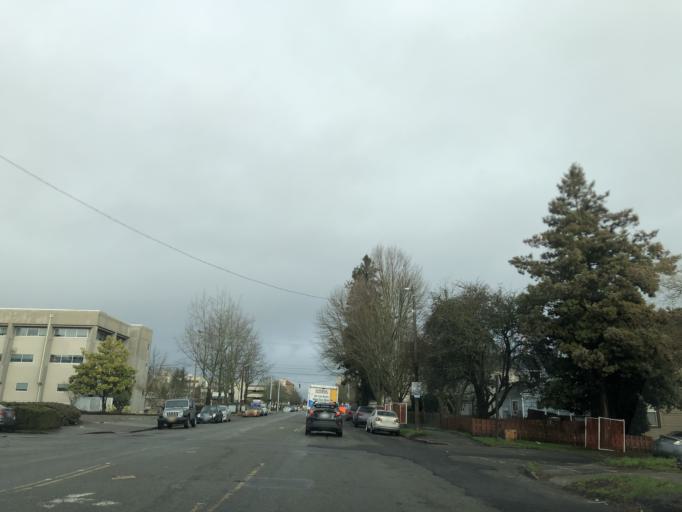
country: US
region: Washington
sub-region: Pierce County
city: Tacoma
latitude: 47.2558
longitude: -122.4525
